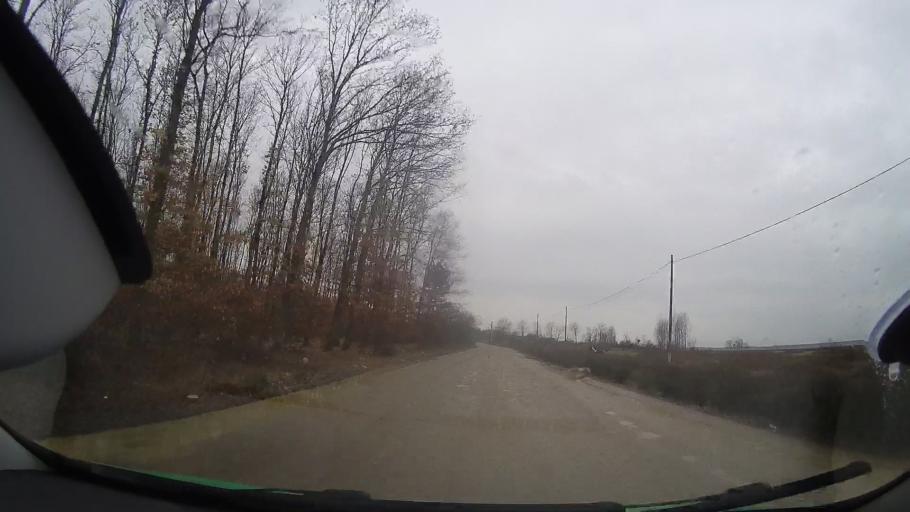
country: RO
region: Bihor
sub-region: Comuna Olcea
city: Olcea
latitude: 46.6883
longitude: 22.0032
